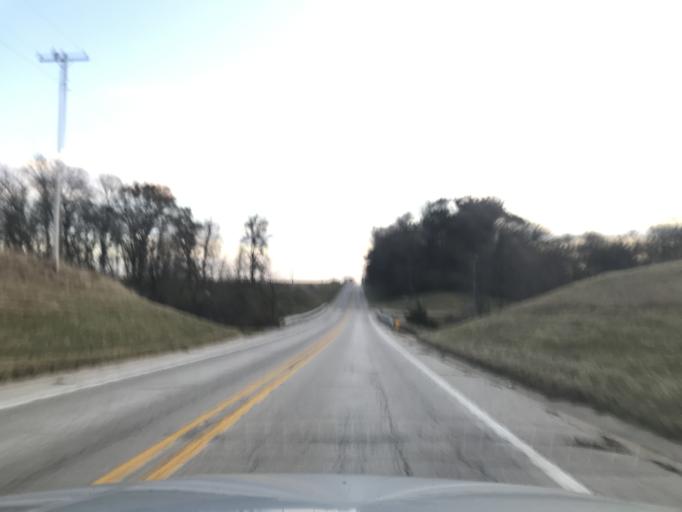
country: US
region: Illinois
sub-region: Henderson County
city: Oquawka
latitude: 40.9538
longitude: -90.8639
